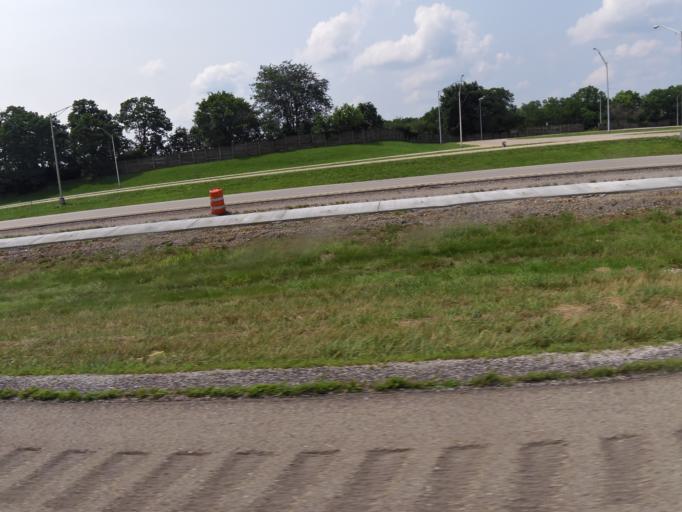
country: US
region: Kentucky
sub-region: Boone County
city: Walton
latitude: 38.8637
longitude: -84.6489
